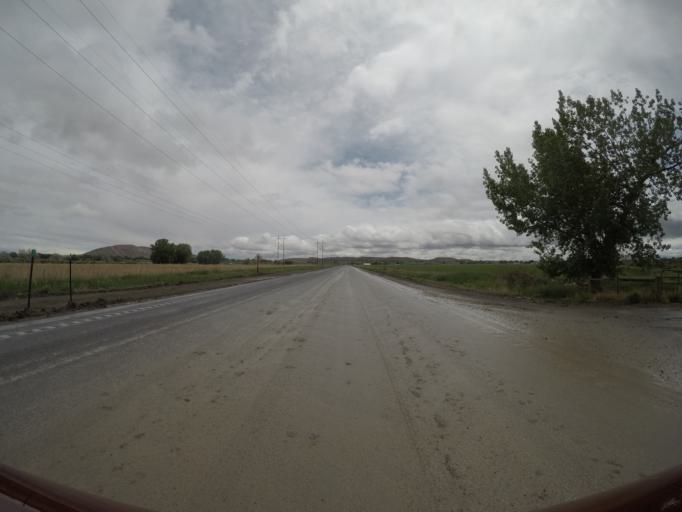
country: US
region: Wyoming
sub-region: Big Horn County
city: Lovell
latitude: 44.8514
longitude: -108.3316
